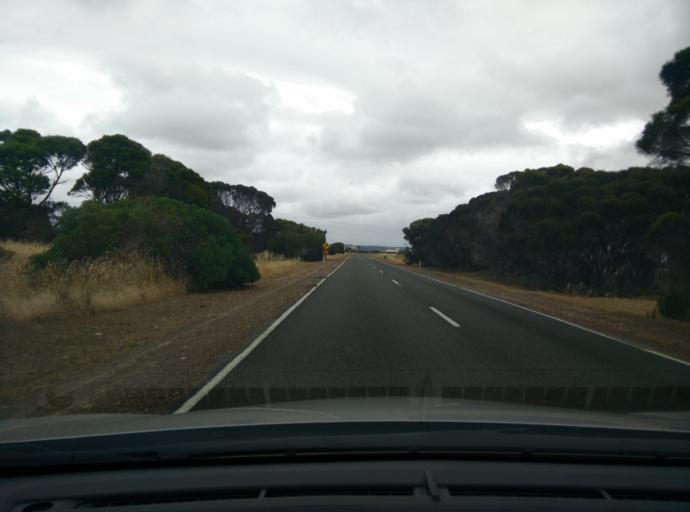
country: AU
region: South Australia
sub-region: Kangaroo Island
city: Kingscote
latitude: -35.6972
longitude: 137.5708
